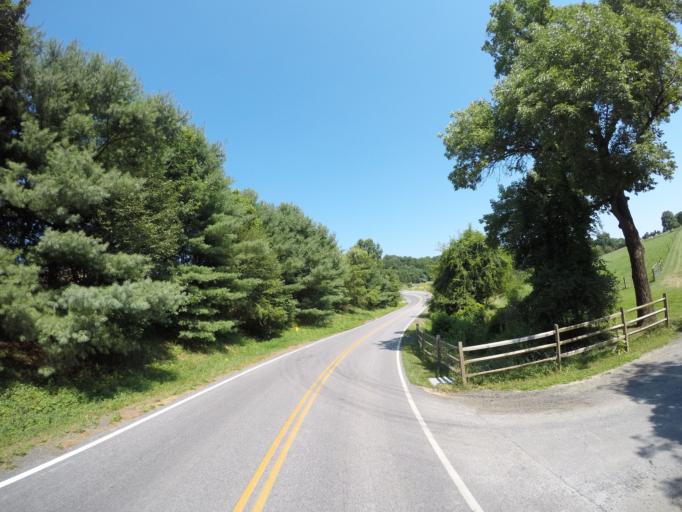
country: US
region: Maryland
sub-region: Frederick County
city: Bartonsville
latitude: 39.3750
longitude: -77.3412
